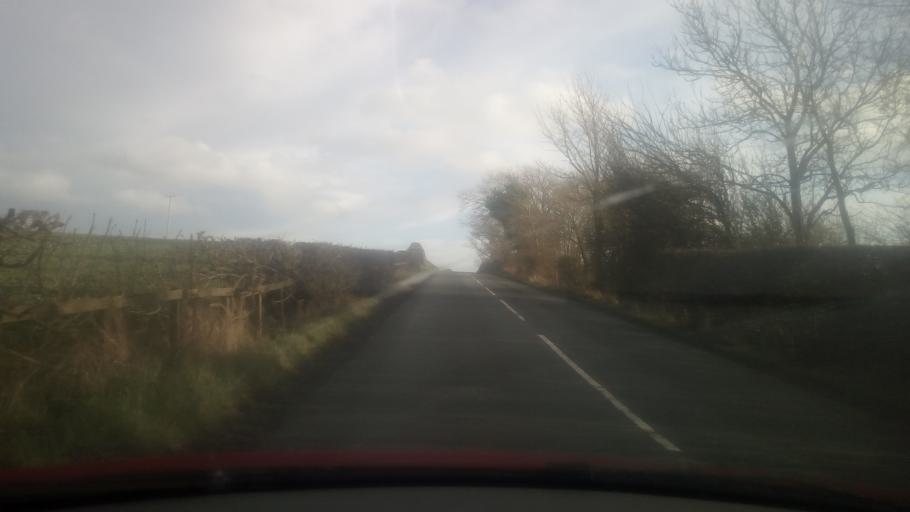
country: GB
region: Scotland
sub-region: The Scottish Borders
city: Coldstream
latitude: 55.7130
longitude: -2.2821
